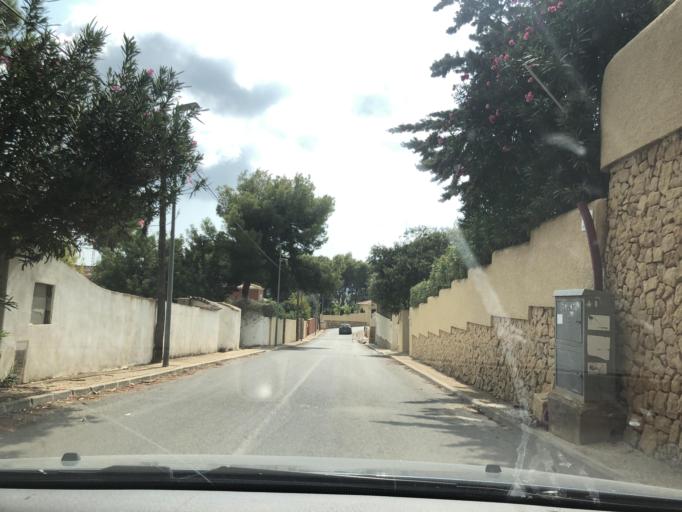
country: ES
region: Valencia
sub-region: Provincia de Alicante
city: Altea
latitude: 38.6367
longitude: -0.0669
